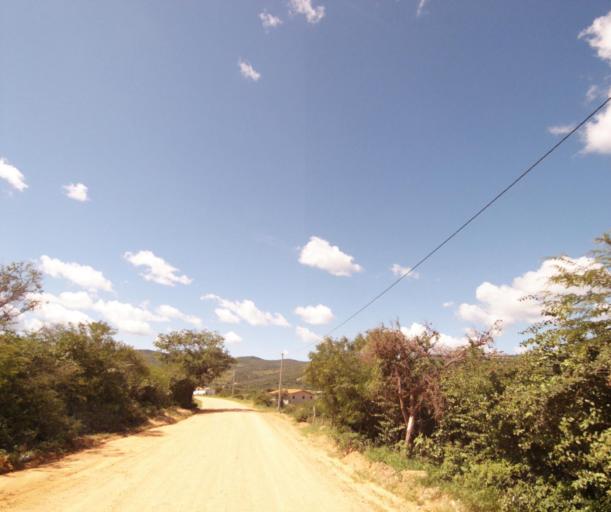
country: BR
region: Bahia
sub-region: Pocoes
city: Pocoes
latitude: -14.2567
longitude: -40.7014
